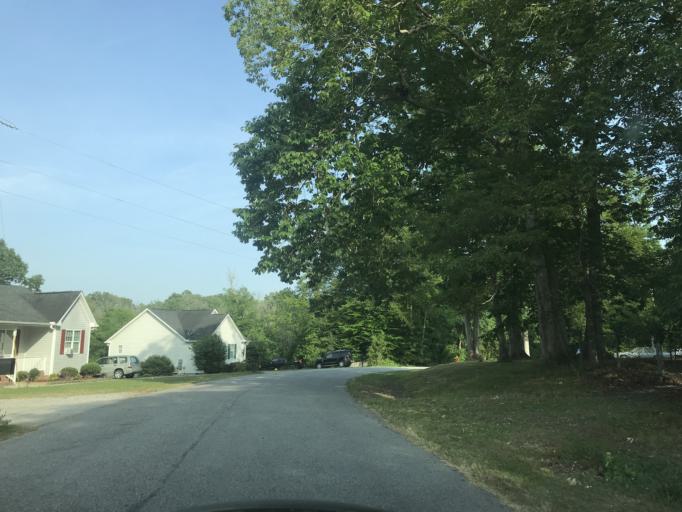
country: US
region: North Carolina
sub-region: Wake County
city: Garner
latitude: 35.7453
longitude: -78.5723
